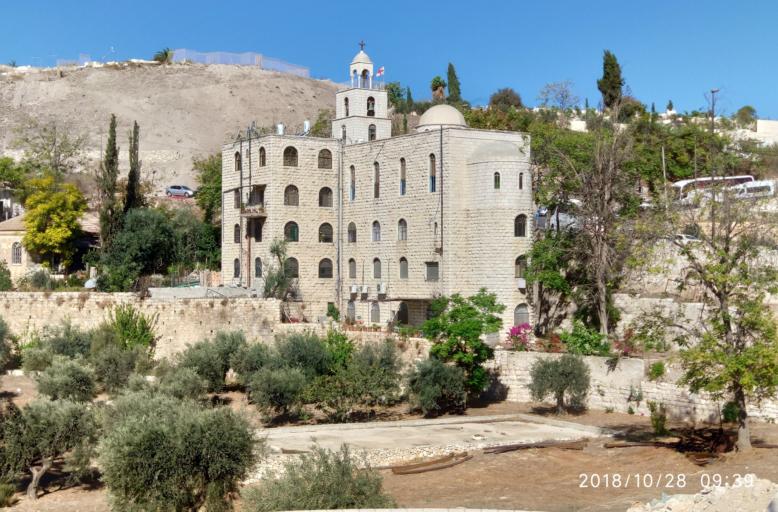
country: PS
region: West Bank
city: Old City
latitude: 31.7794
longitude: 35.2392
